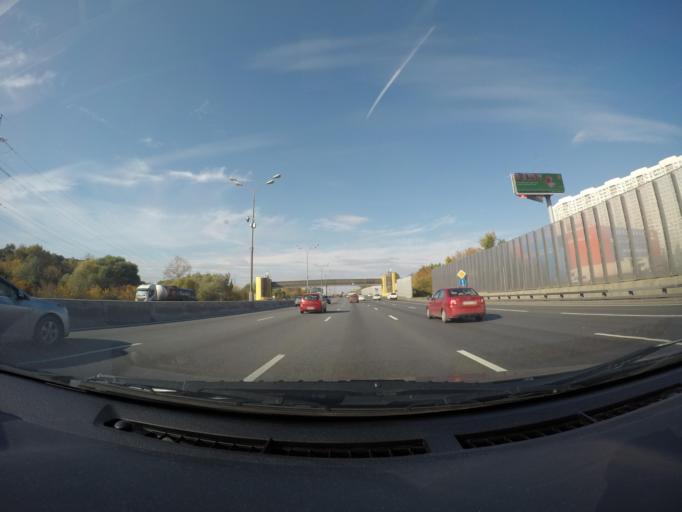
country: RU
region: Moscow
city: Yaroslavskiy
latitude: 55.8895
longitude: 37.7121
